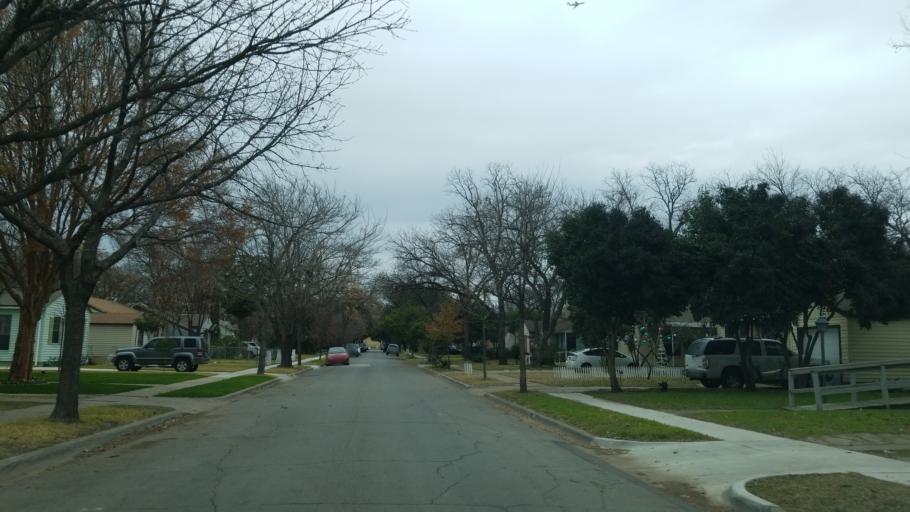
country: US
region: Texas
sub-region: Dallas County
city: Highland Park
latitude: 32.8231
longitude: -96.8329
